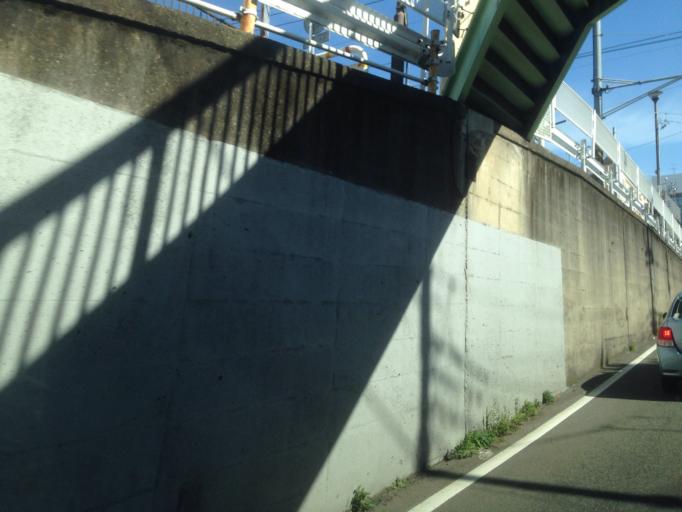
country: JP
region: Tokyo
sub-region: Machida-shi
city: Machida
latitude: 35.5675
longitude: 139.3975
